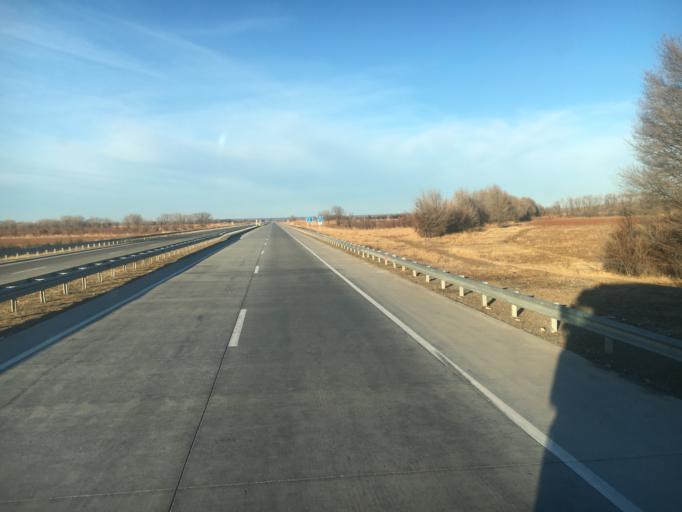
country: KZ
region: Ongtustik Qazaqstan
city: Turkestan
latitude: 43.1556
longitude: 68.5642
